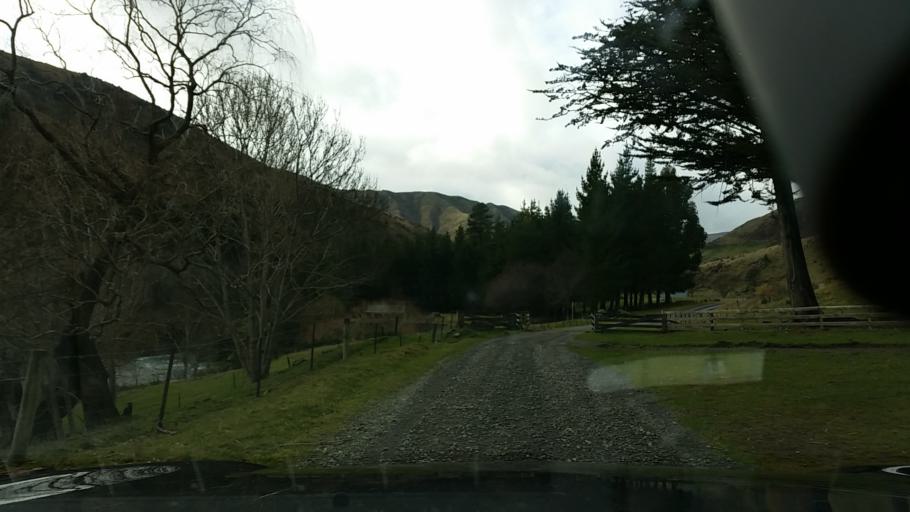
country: NZ
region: Tasman
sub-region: Tasman District
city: Brightwater
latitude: -41.7360
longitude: 173.4215
